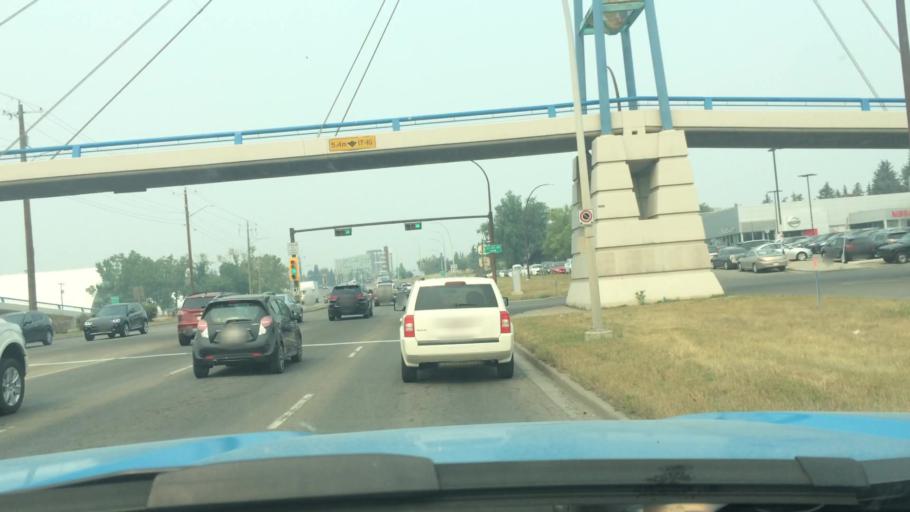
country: CA
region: Alberta
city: Calgary
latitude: 51.0705
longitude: -114.1182
